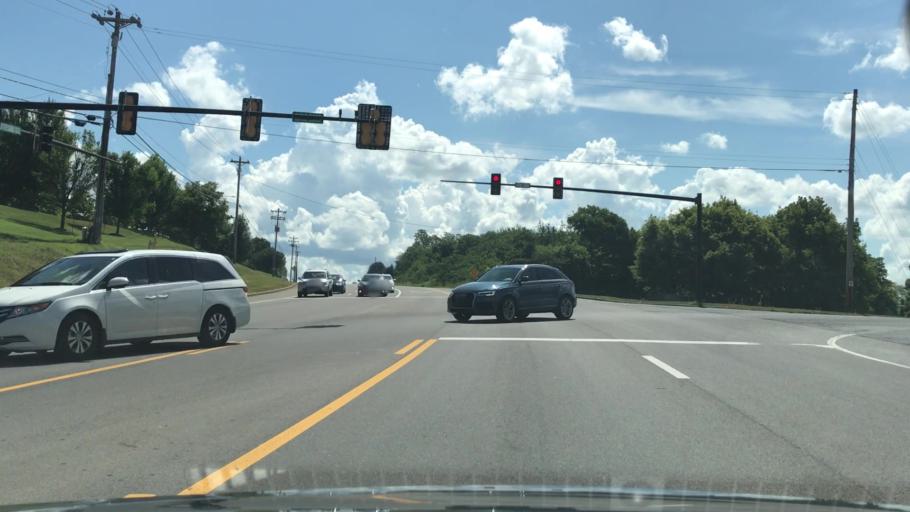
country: US
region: Tennessee
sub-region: Williamson County
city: Franklin
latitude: 35.9042
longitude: -86.8008
